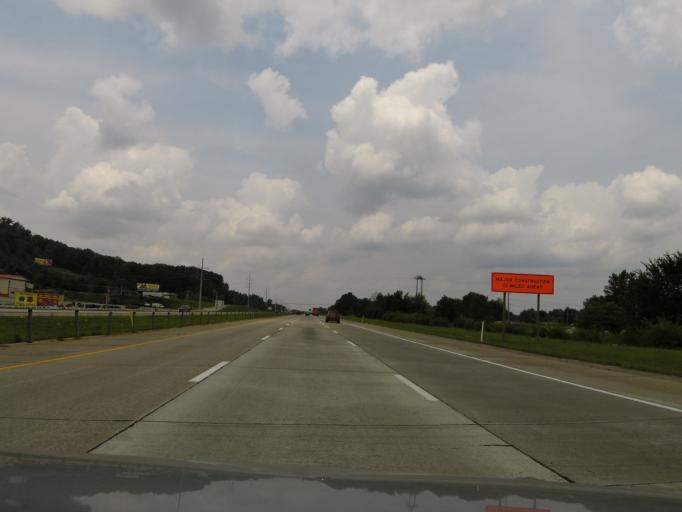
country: US
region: Kentucky
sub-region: Bullitt County
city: Hillview
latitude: 38.0727
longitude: -85.6999
